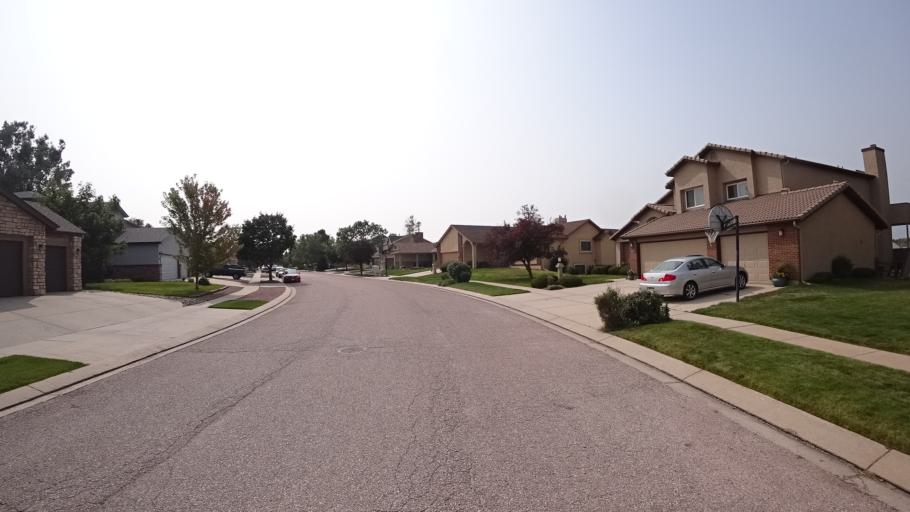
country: US
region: Colorado
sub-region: El Paso County
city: Cimarron Hills
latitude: 38.9192
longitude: -104.7437
